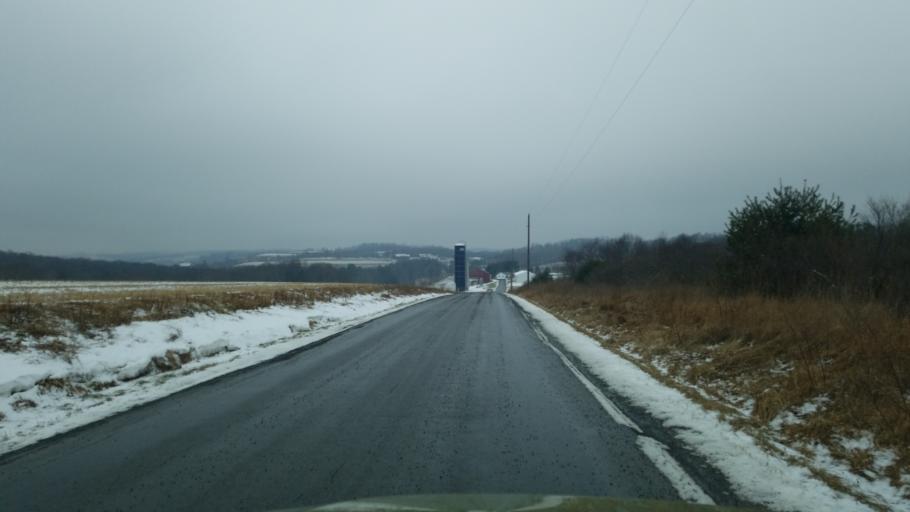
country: US
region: Pennsylvania
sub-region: Jefferson County
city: Sykesville
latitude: 41.0356
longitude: -78.7759
